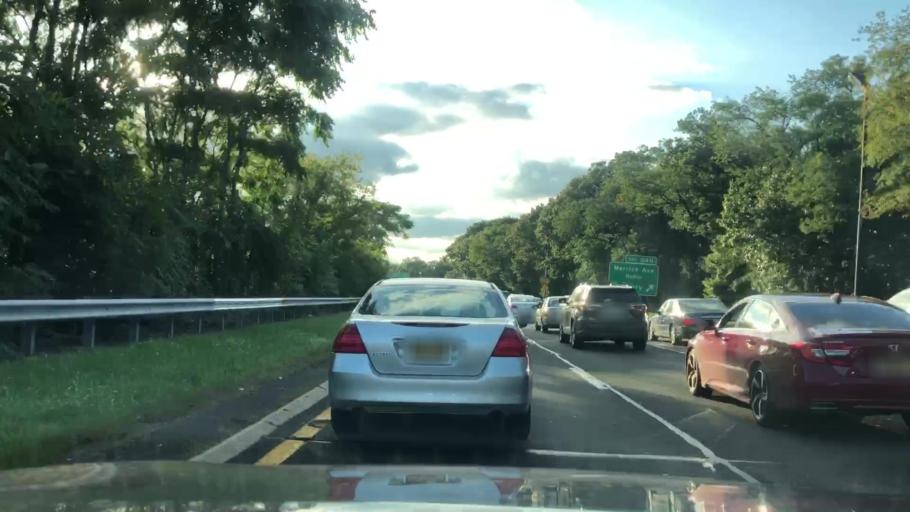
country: US
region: New York
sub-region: Nassau County
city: North Merrick
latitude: 40.6902
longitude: -73.5582
